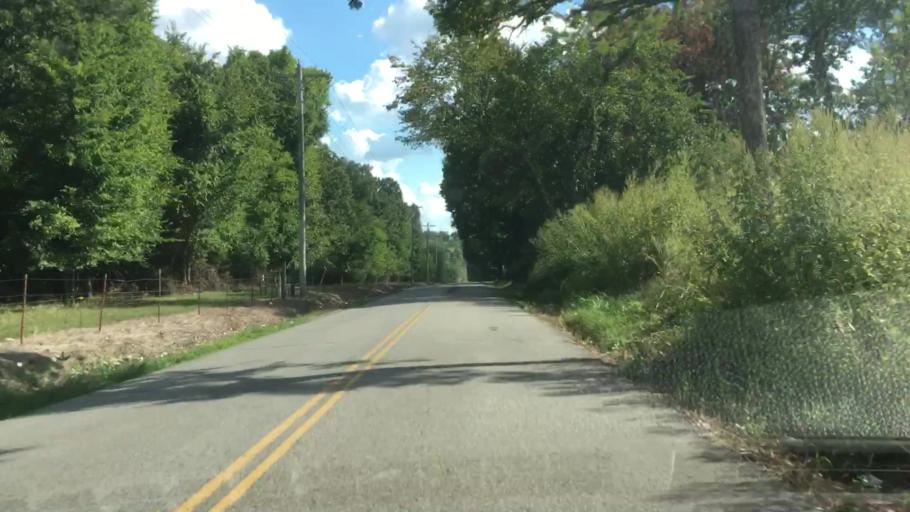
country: US
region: Oklahoma
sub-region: Cherokee County
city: Park Hill
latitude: 35.8040
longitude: -95.0739
